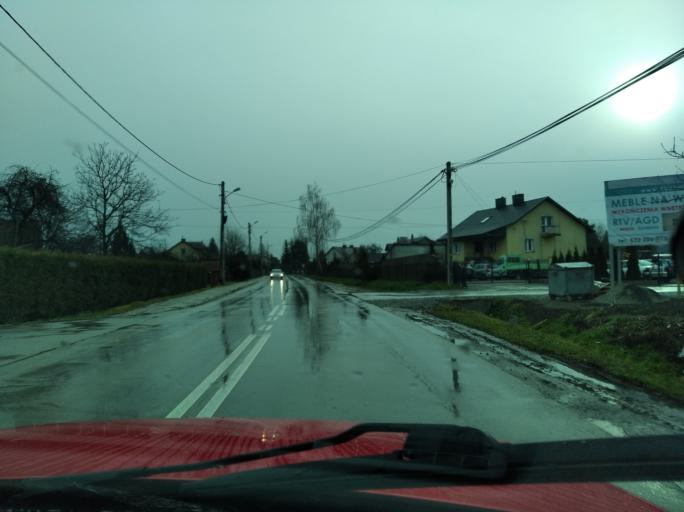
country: PL
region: Subcarpathian Voivodeship
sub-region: Rzeszow
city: Rzeszow
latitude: 50.0014
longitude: 21.9908
